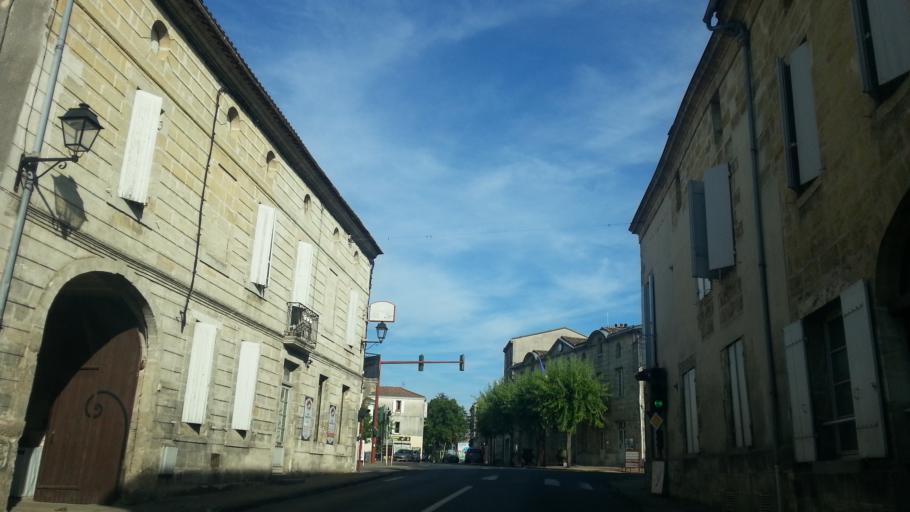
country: FR
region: Aquitaine
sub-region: Departement de la Gironde
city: Castres-Gironde
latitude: 44.6969
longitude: -0.4457
